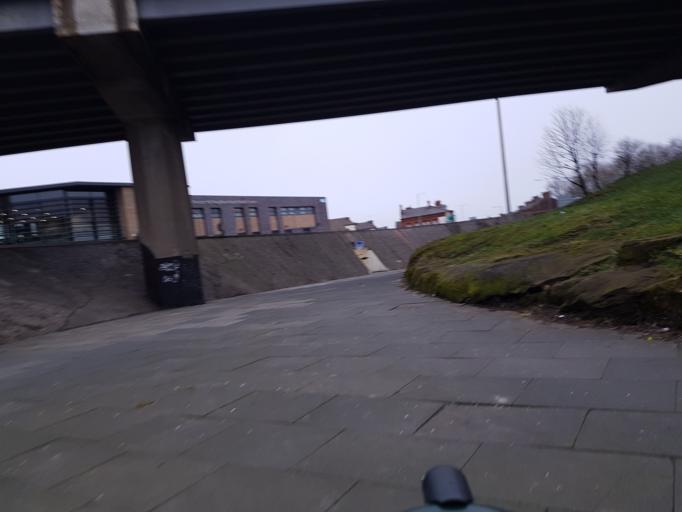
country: GB
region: England
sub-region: Sefton
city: Litherland
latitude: 53.4473
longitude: -2.9673
